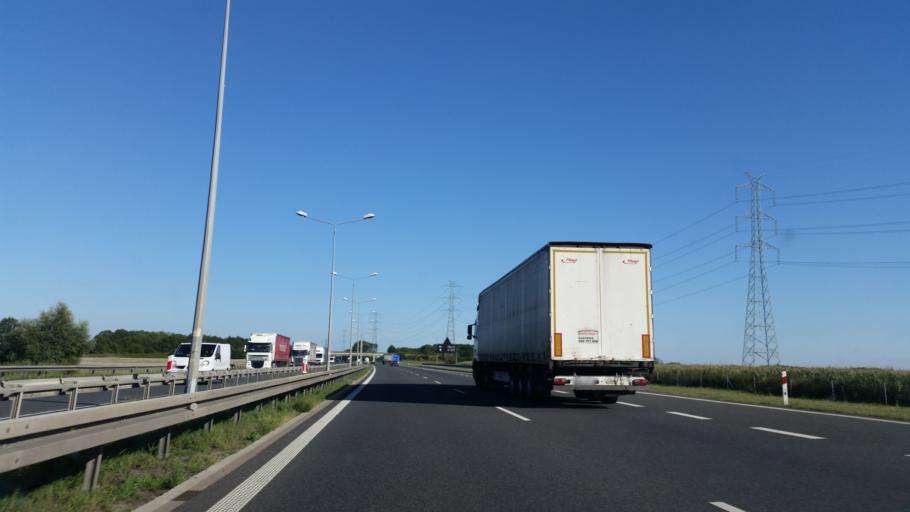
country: PL
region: Opole Voivodeship
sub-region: Powiat brzeski
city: Grodkow
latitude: 50.7799
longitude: 17.3524
